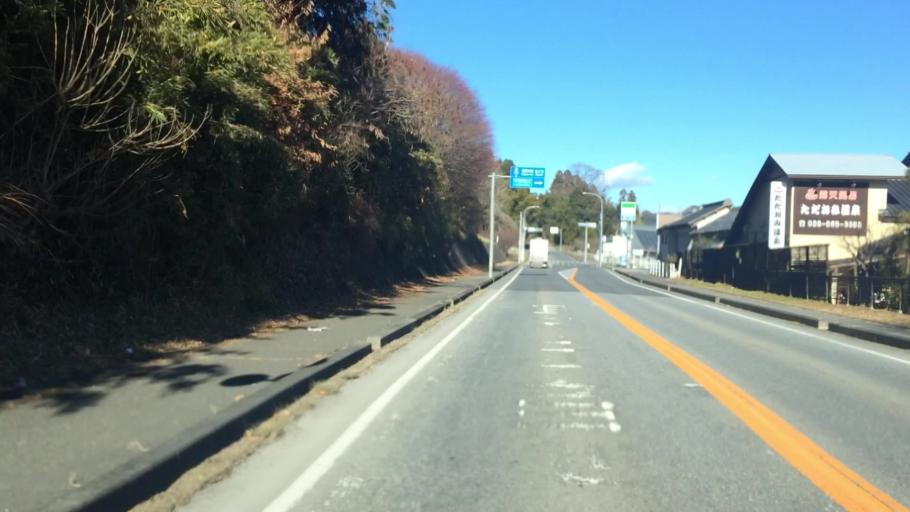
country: JP
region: Tochigi
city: Utsunomiya-shi
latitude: 36.6387
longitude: 139.8338
